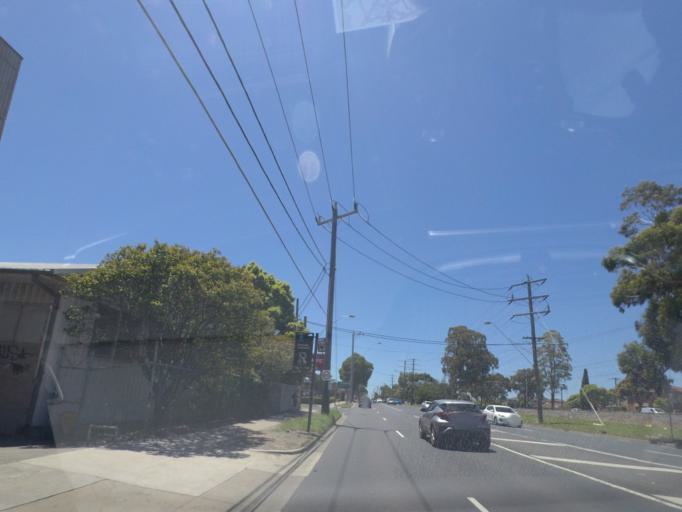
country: AU
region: Victoria
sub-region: Darebin
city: Reservoir
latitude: -37.7136
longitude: 145.0081
